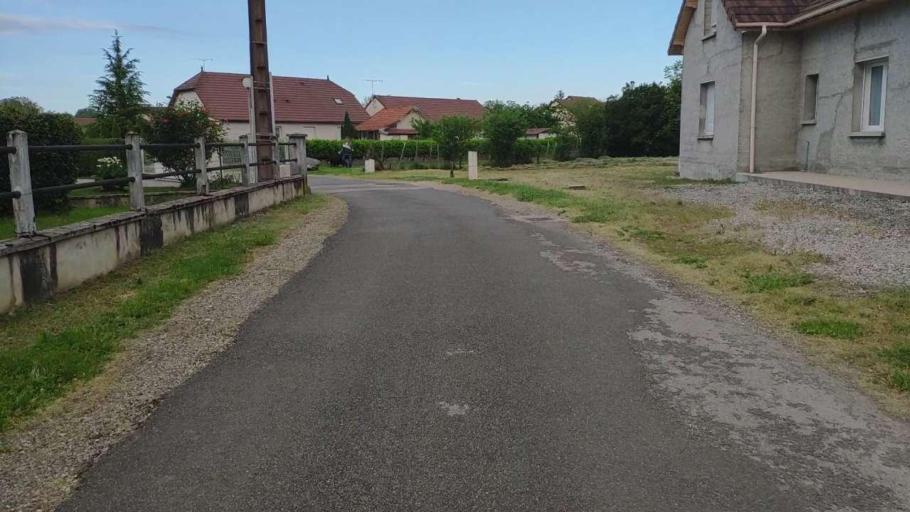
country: FR
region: Franche-Comte
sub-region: Departement du Jura
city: Bletterans
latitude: 46.7449
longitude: 5.4483
